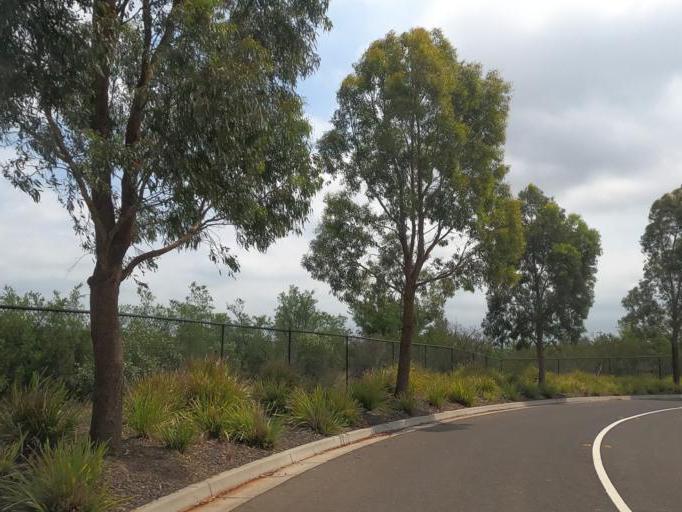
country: AU
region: Victoria
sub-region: Hume
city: Attwood
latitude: -37.6731
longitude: 144.8773
